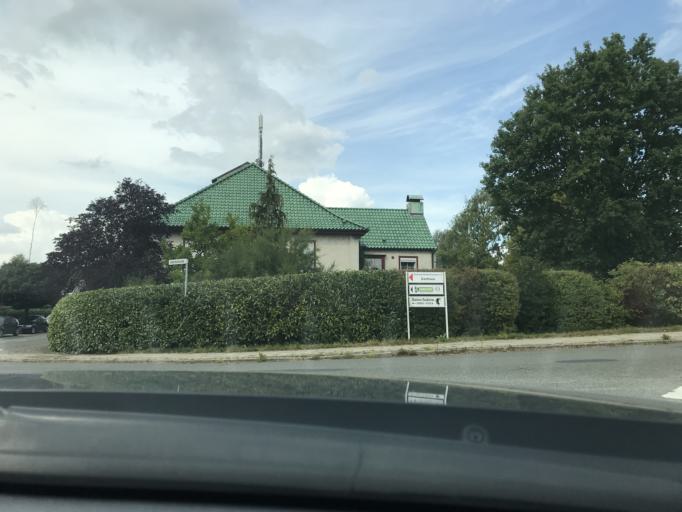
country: DE
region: Lower Saxony
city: Suderburg
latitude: 52.9045
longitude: 10.4354
